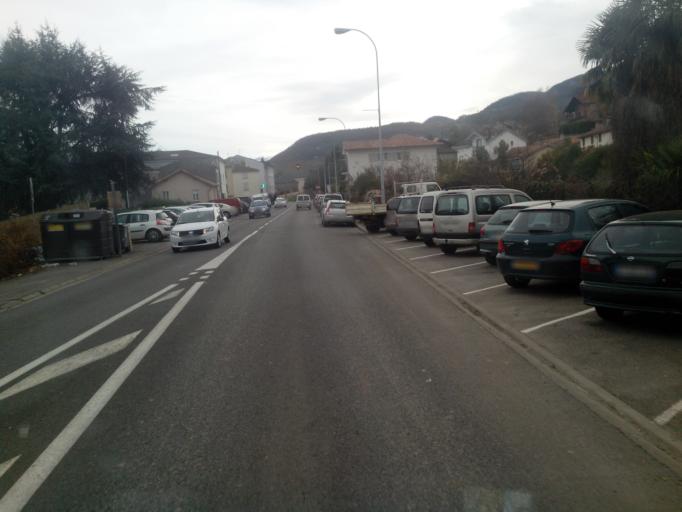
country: FR
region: Midi-Pyrenees
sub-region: Departement de l'Ariege
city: Saint-Girons
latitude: 42.9848
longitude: 1.1408
